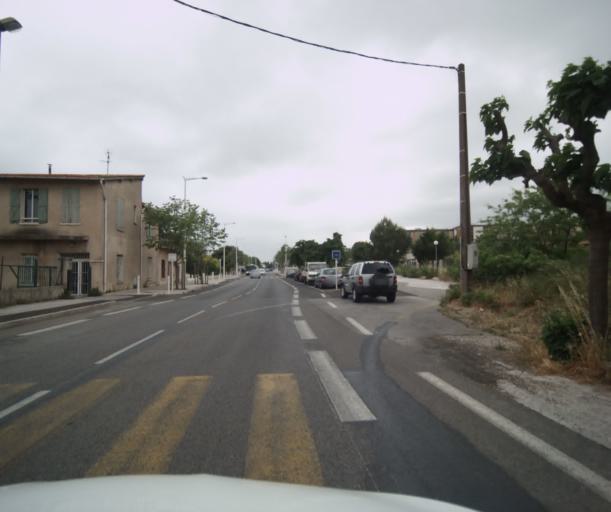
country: FR
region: Provence-Alpes-Cote d'Azur
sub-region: Departement du Var
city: La Seyne-sur-Mer
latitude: 43.1282
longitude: 5.8839
